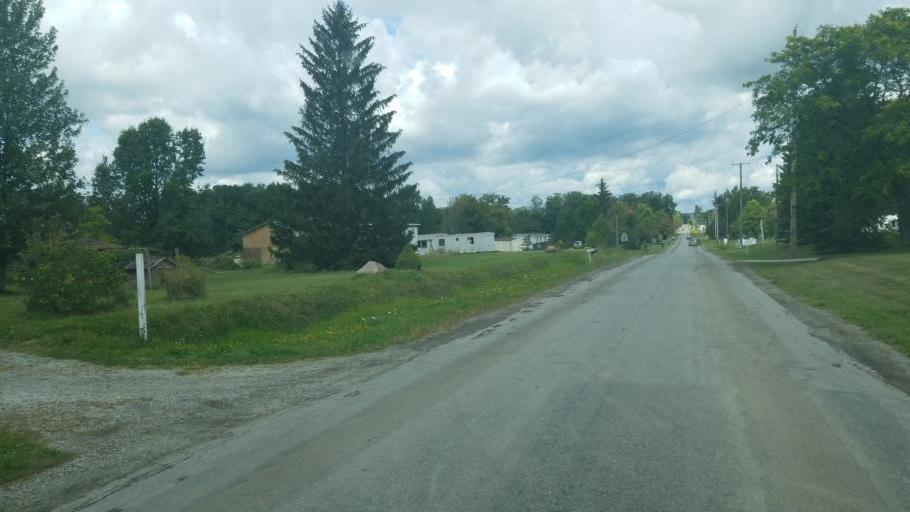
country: US
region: Ohio
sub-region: Geauga County
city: Middlefield
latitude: 41.4416
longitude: -81.0806
